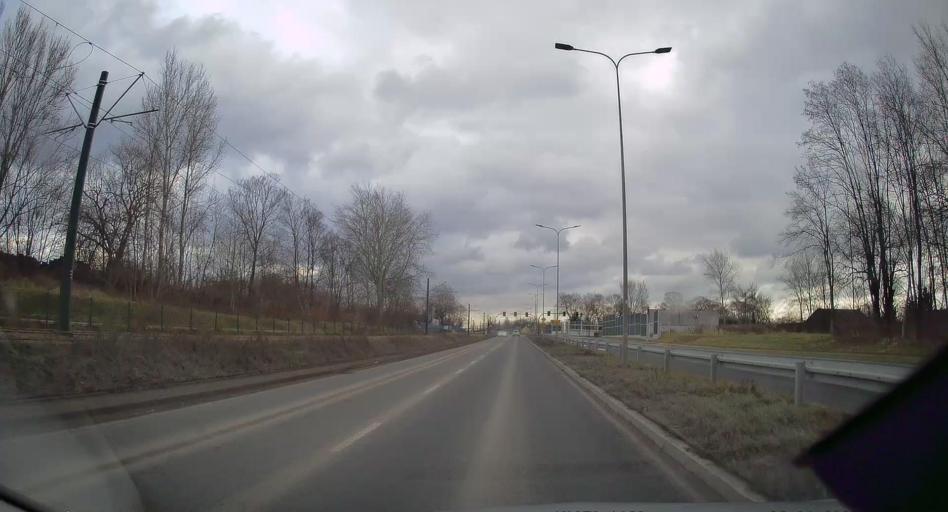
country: PL
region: Lesser Poland Voivodeship
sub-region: Powiat wielicki
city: Wegrzce Wielkie
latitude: 50.0724
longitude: 20.1127
